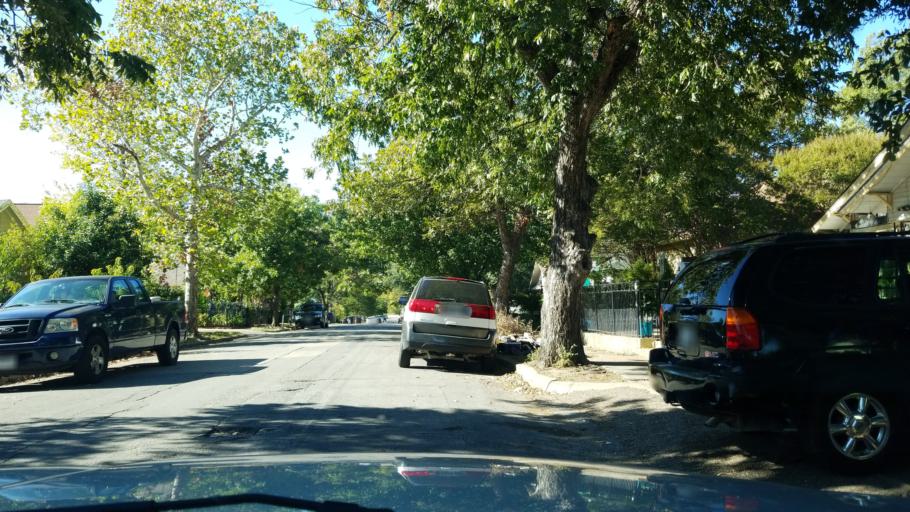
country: US
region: Texas
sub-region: Dallas County
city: Highland Park
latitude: 32.8030
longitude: -96.7455
